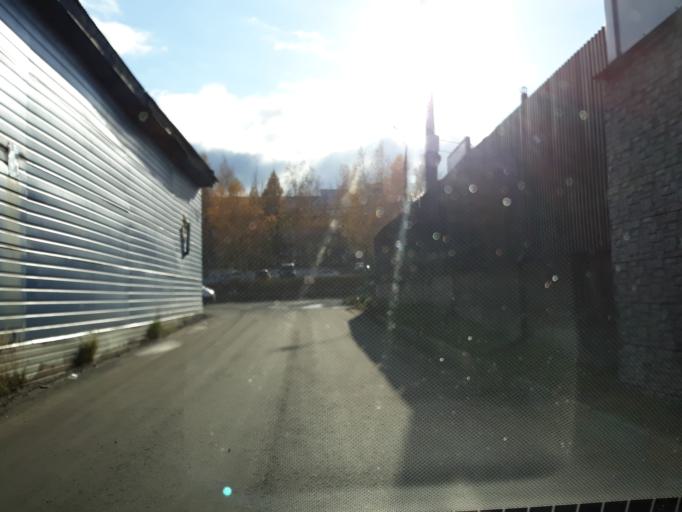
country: RU
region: Nizjnij Novgorod
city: Nizhniy Novgorod
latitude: 56.2385
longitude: 44.0057
